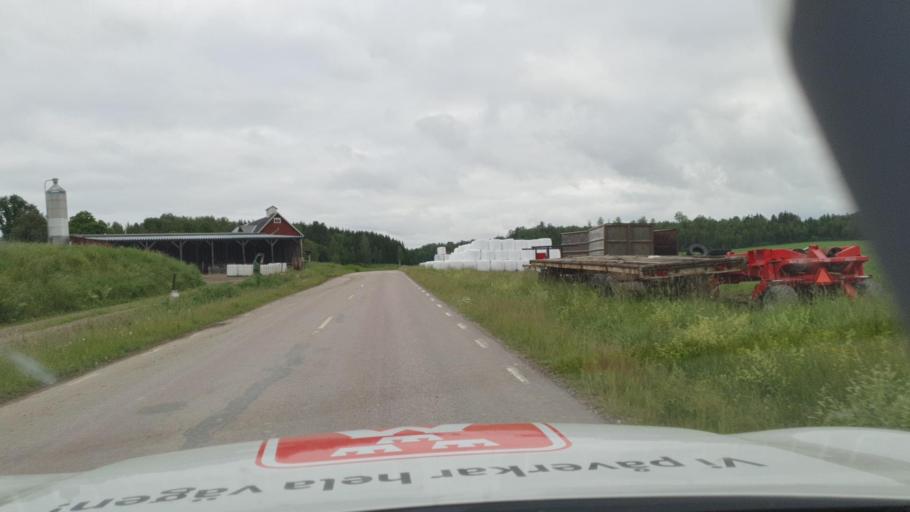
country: SE
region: Vaermland
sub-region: Kils Kommun
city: Kil
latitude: 59.5614
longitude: 13.2895
